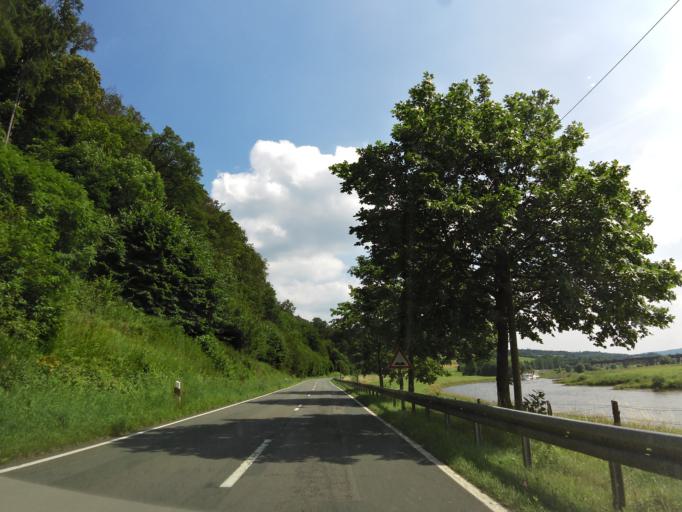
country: DE
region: Lower Saxony
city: Furstenberg
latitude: 51.7072
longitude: 9.4007
